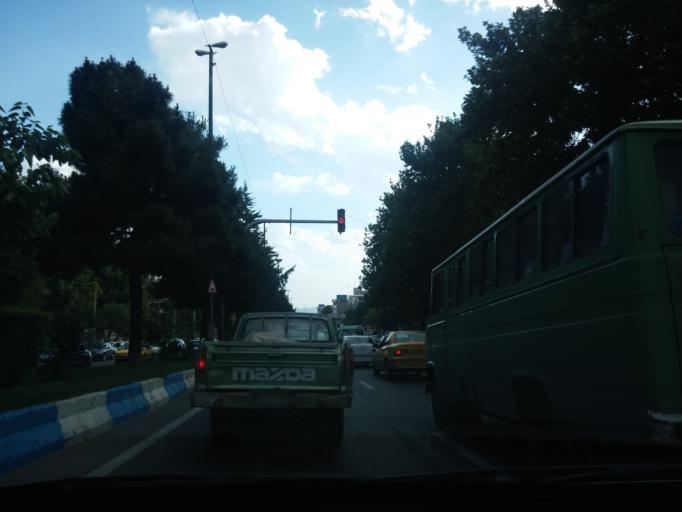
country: IR
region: Tehran
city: Damavand
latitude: 35.7340
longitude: 51.9072
